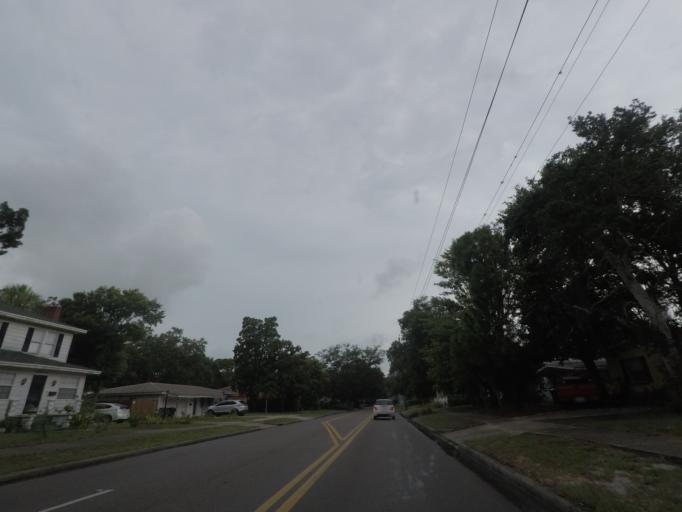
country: US
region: Florida
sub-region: Pinellas County
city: Treasure Island
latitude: 27.7923
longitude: -82.7521
